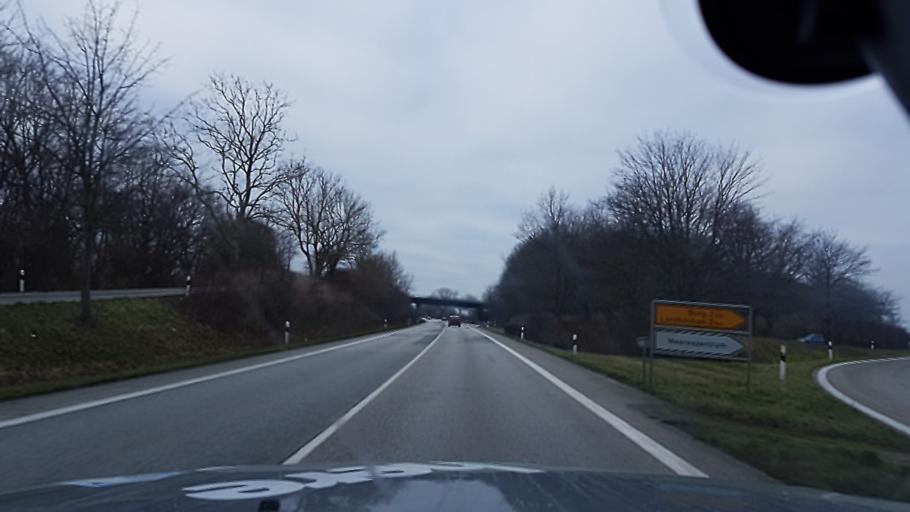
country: DE
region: Schleswig-Holstein
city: Fehmarn
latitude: 54.4467
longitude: 11.1724
